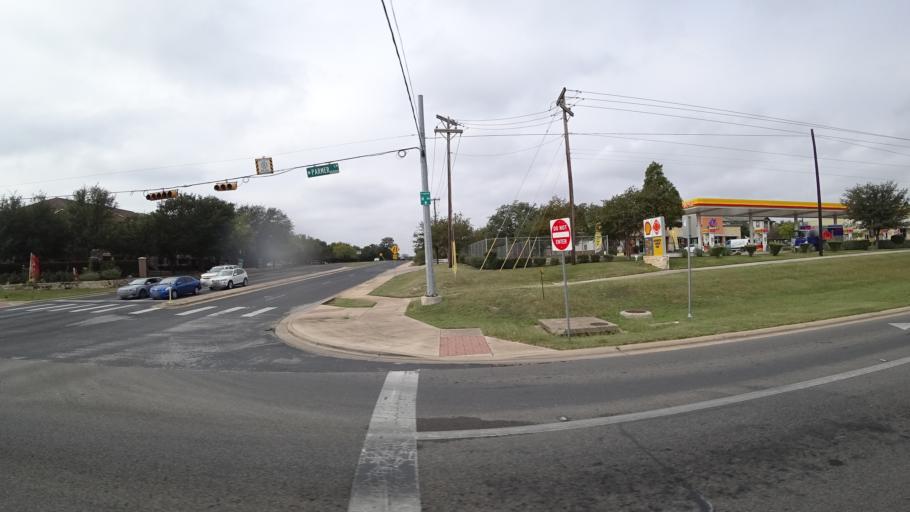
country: US
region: Texas
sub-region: Williamson County
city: Brushy Creek
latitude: 30.4882
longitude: -97.7715
